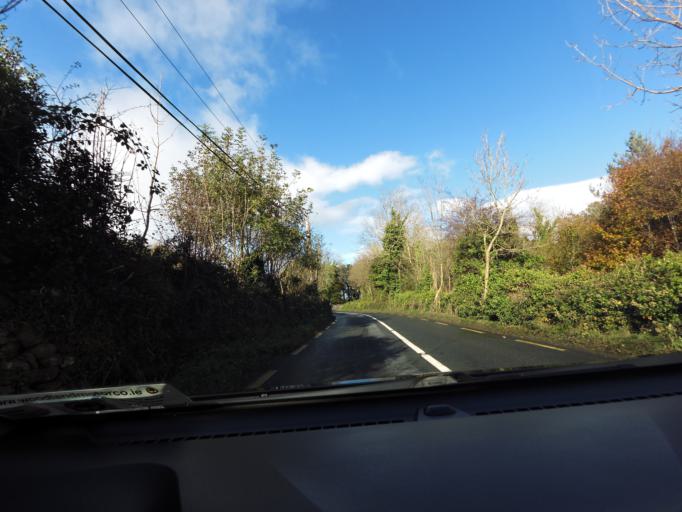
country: IE
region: Connaught
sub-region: Maigh Eo
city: Westport
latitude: 53.8120
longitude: -9.5336
